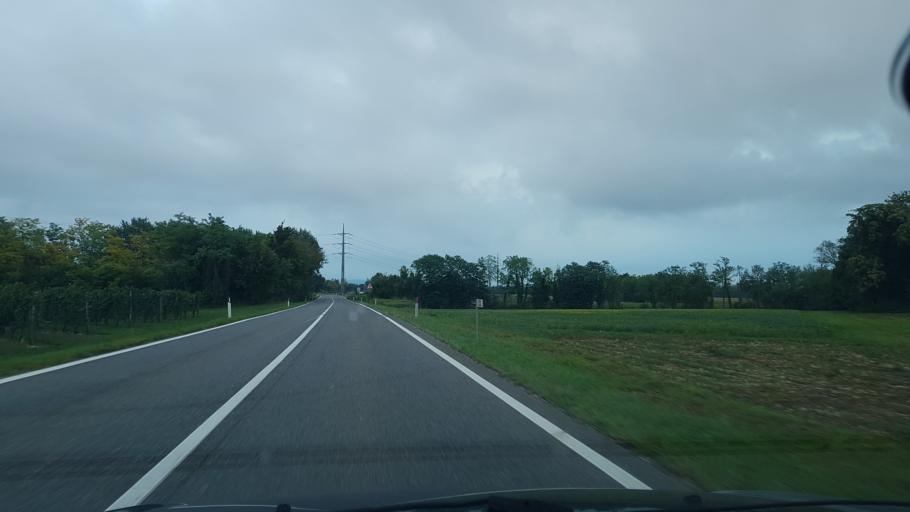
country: IT
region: Friuli Venezia Giulia
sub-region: Provincia di Udine
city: San Vito al Torre
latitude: 45.8921
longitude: 13.3862
